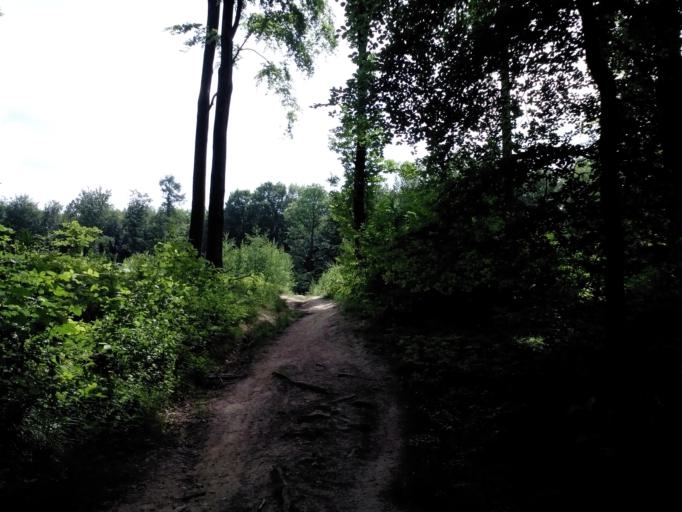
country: BE
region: Flanders
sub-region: Provincie Vlaams-Brabant
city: Oud-Heverlee
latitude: 50.7957
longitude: 4.6701
